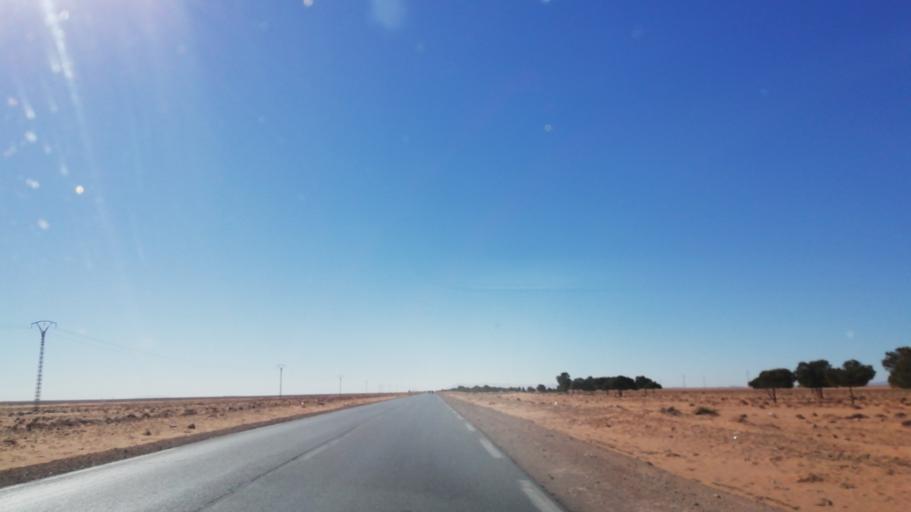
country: DZ
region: Saida
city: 'Ain el Hadjar
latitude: 33.9791
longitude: 0.0270
